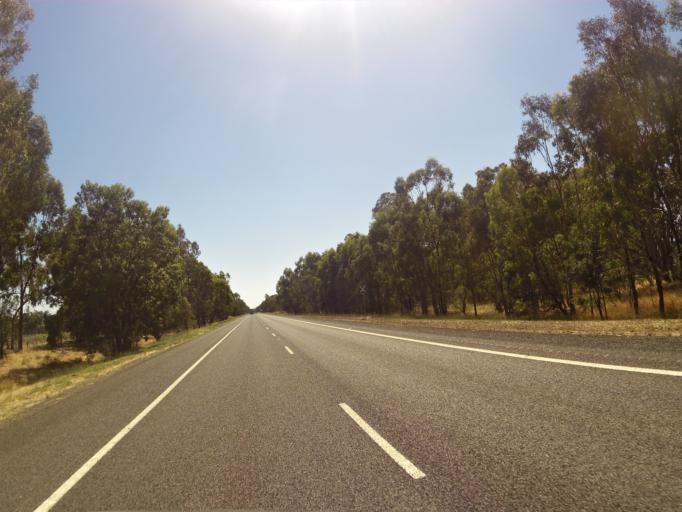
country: AU
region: Victoria
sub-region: Greater Shepparton
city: Shepparton
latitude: -36.8035
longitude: 145.4676
